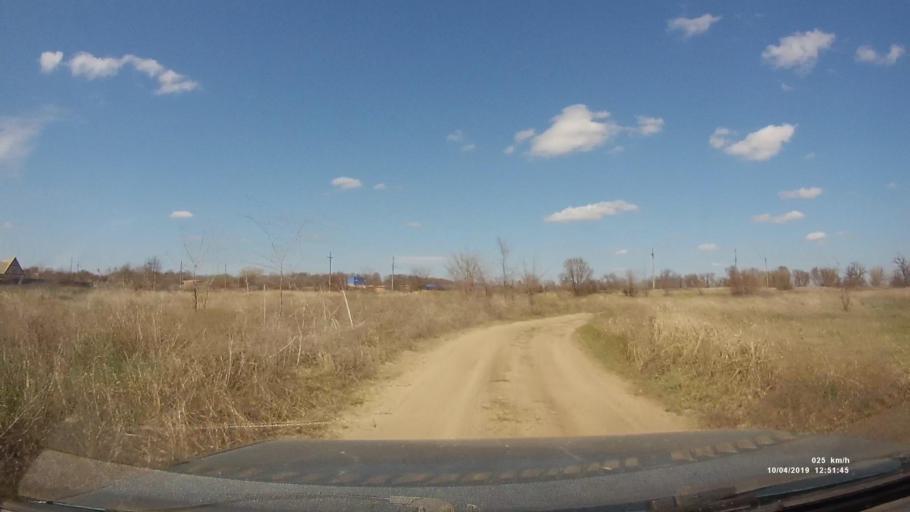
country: RU
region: Rostov
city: Kamensk-Shakhtinskiy
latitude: 48.3602
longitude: 40.2166
